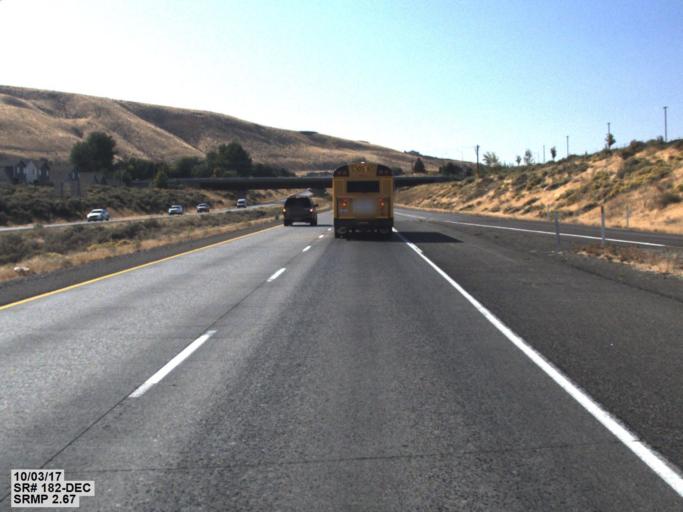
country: US
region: Washington
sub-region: Benton County
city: Richland
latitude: 46.2531
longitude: -119.3090
